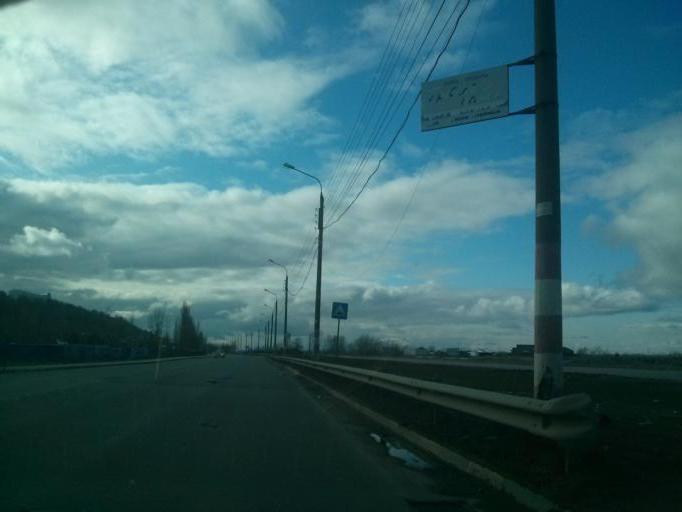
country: RU
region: Nizjnij Novgorod
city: Nizhniy Novgorod
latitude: 56.3274
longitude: 44.0410
